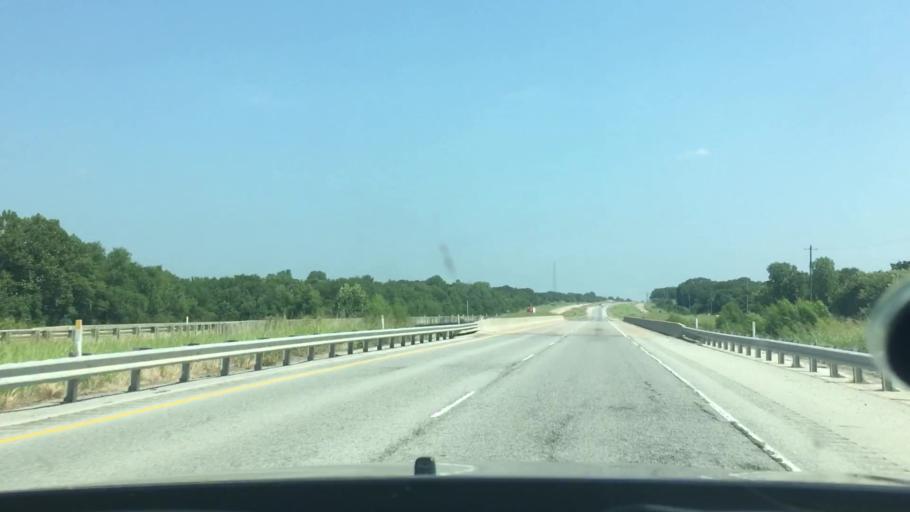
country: US
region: Oklahoma
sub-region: Atoka County
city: Atoka
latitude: 34.2585
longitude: -96.2117
